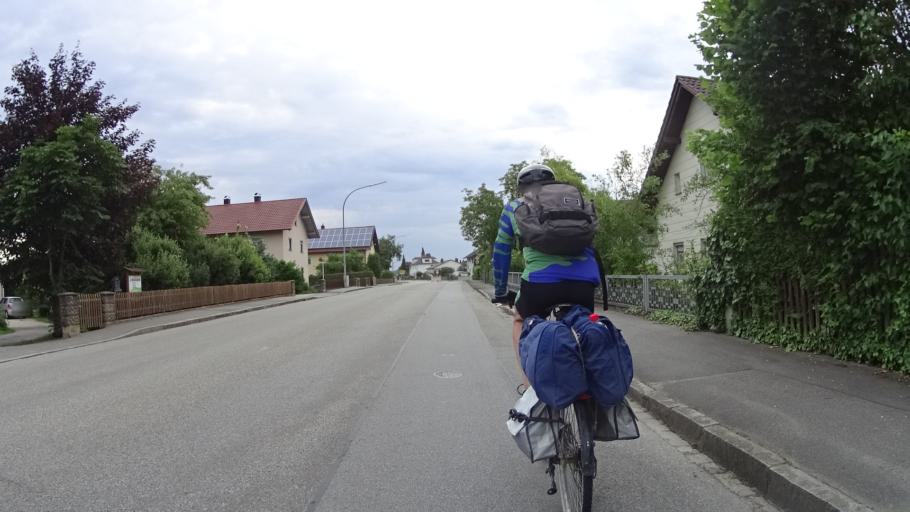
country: DE
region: Bavaria
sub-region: Lower Bavaria
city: Parkstetten
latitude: 48.9166
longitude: 12.6009
